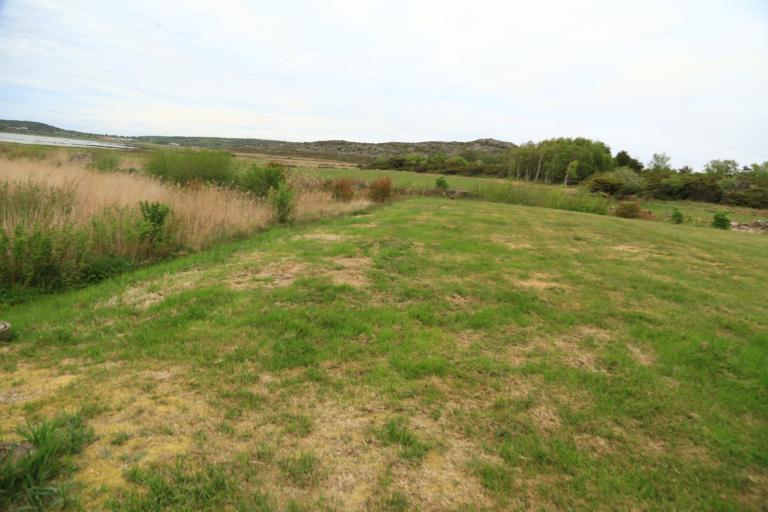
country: SE
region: Halland
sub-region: Varbergs Kommun
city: Varberg
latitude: 57.1527
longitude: 12.2278
